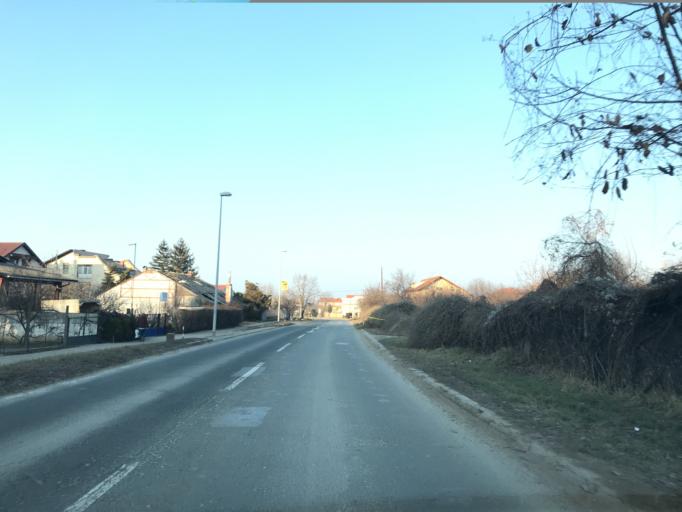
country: RS
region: Autonomna Pokrajina Vojvodina
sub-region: Juznobacki Okrug
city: Petrovaradin
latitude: 45.2241
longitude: 19.8557
